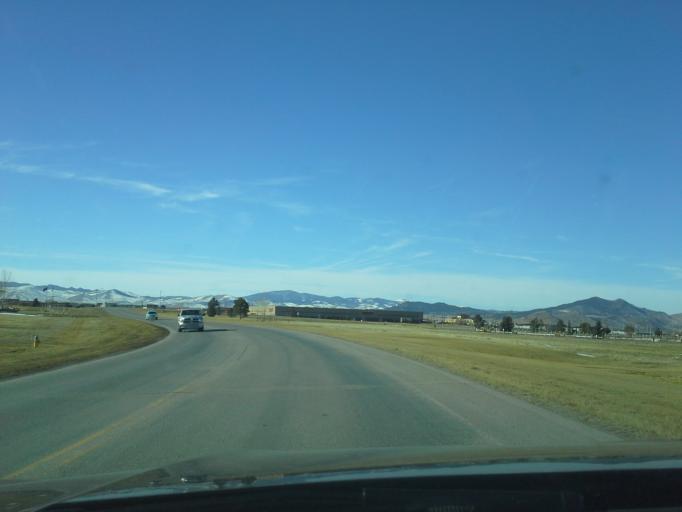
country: US
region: Montana
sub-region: Lewis and Clark County
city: Helena
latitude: 46.6129
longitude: -111.9952
